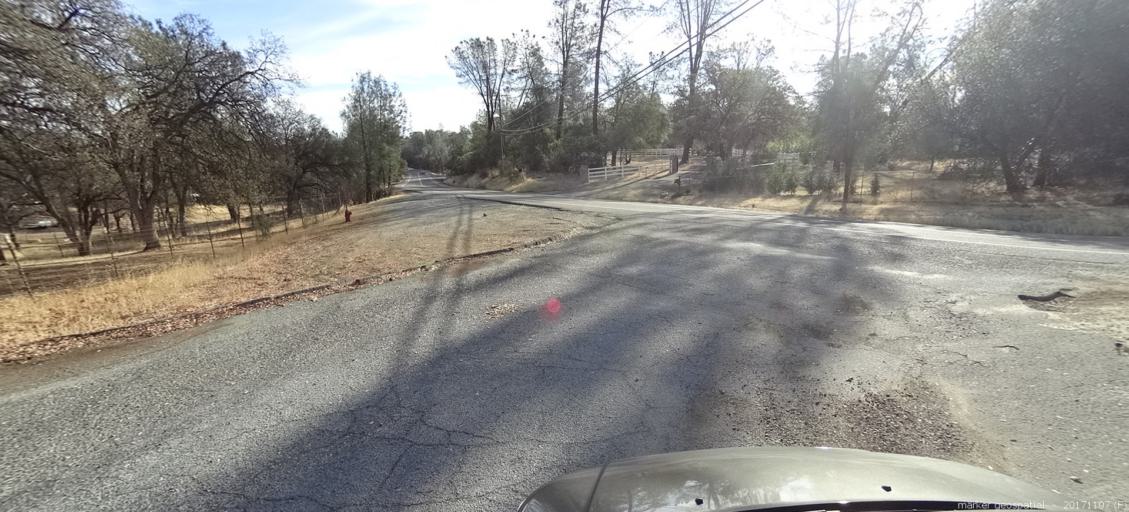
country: US
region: California
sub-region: Shasta County
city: Shasta
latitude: 40.5531
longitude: -122.4502
